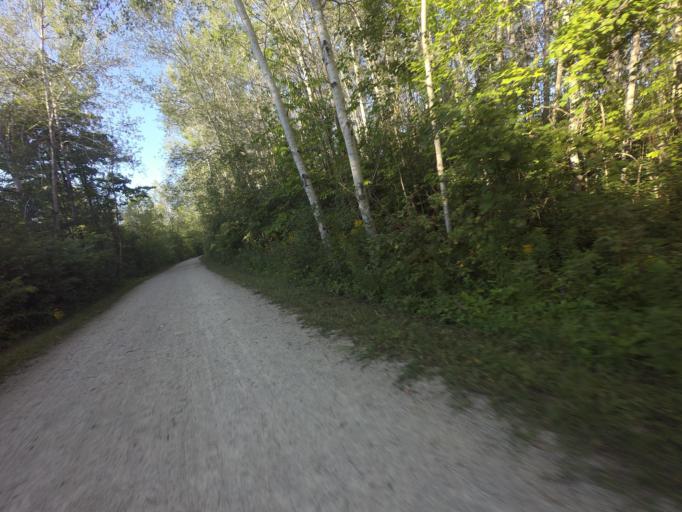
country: CA
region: Ontario
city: Orangeville
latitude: 43.8086
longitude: -79.9326
